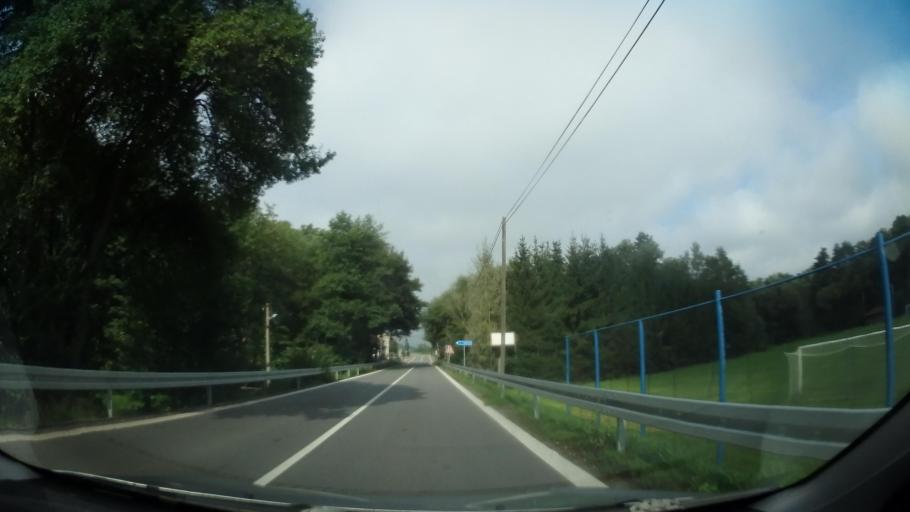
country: CZ
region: Central Bohemia
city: Bystrice
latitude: 49.7582
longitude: 14.6626
